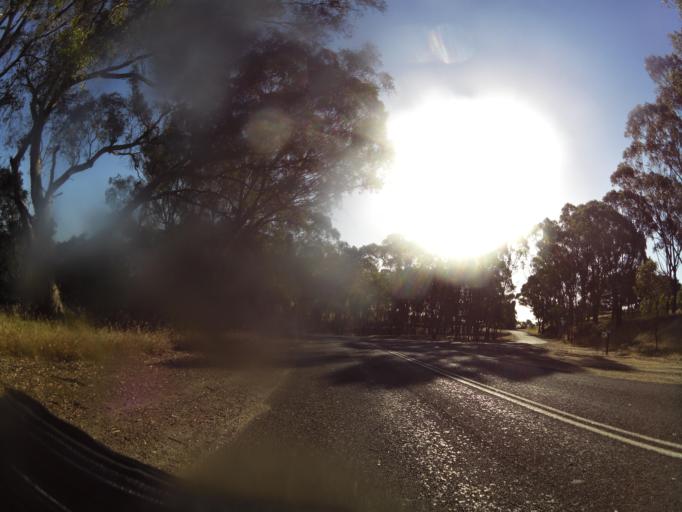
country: AU
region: Victoria
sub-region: Murrindindi
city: Kinglake West
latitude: -37.0219
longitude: 145.1044
